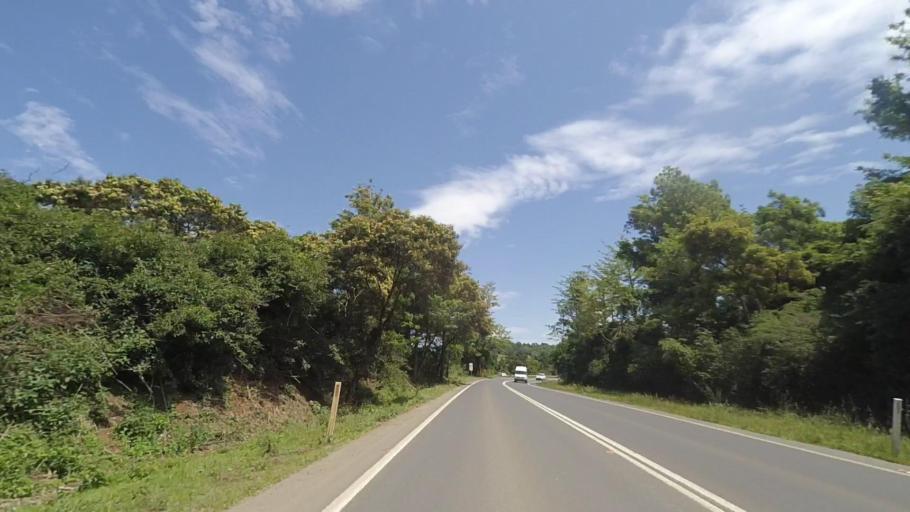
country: AU
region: New South Wales
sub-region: Kiama
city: Gerringong
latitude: -34.7467
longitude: 150.7574
